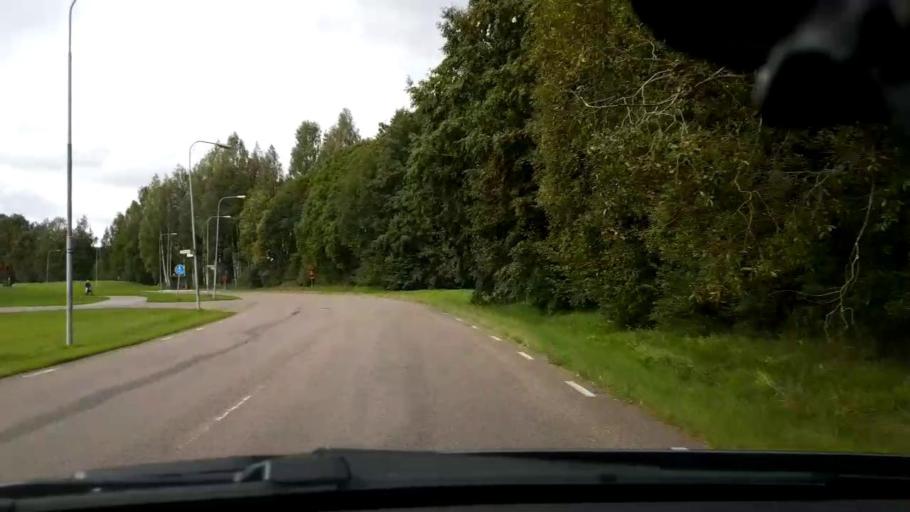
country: SE
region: Dalarna
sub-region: Borlange Kommun
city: Borlaenge
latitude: 60.4861
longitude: 15.4025
